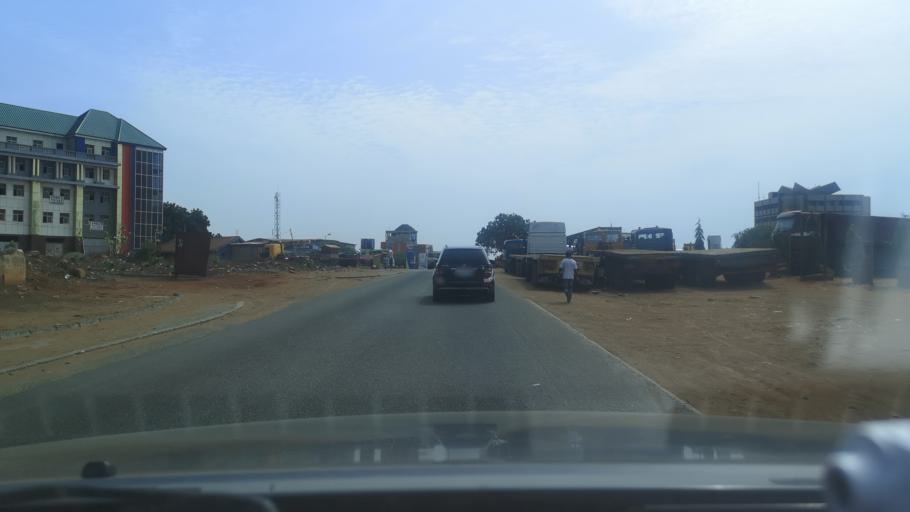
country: GH
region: Greater Accra
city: Tema
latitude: 5.6346
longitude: -0.0008
